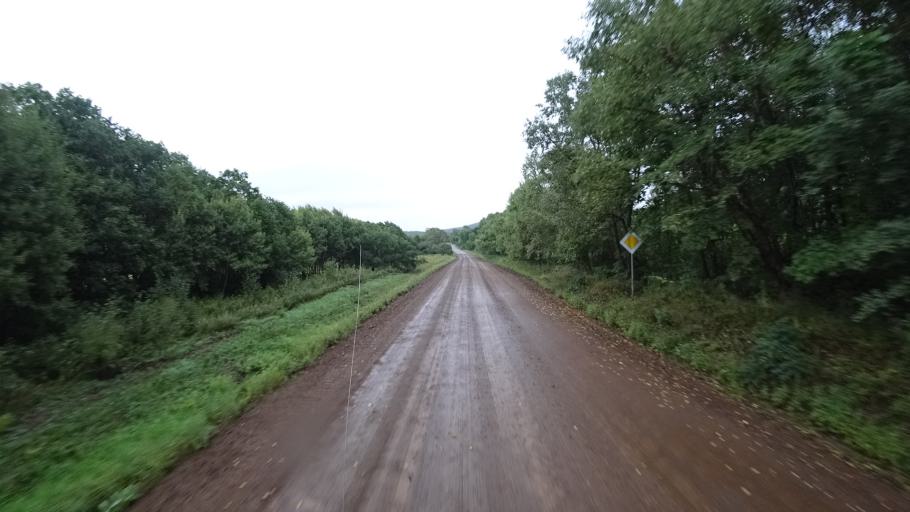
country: RU
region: Primorskiy
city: Monastyrishche
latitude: 44.2743
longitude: 132.4468
